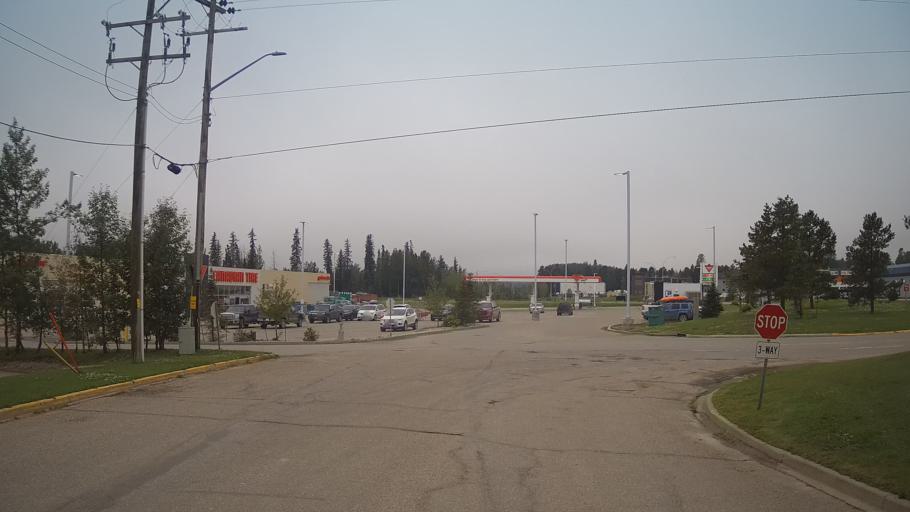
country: CA
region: Alberta
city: Edson
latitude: 53.5753
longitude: -116.4512
